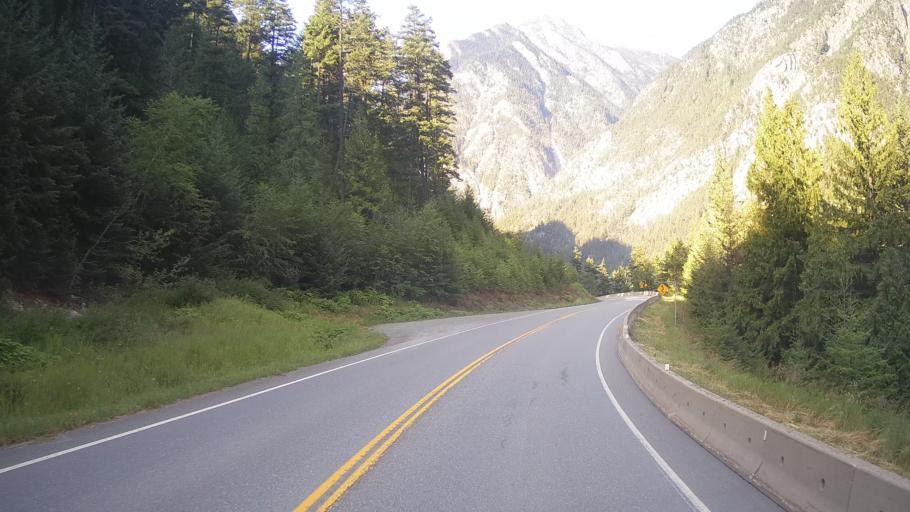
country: CA
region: British Columbia
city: Lillooet
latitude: 50.6317
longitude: -122.0900
